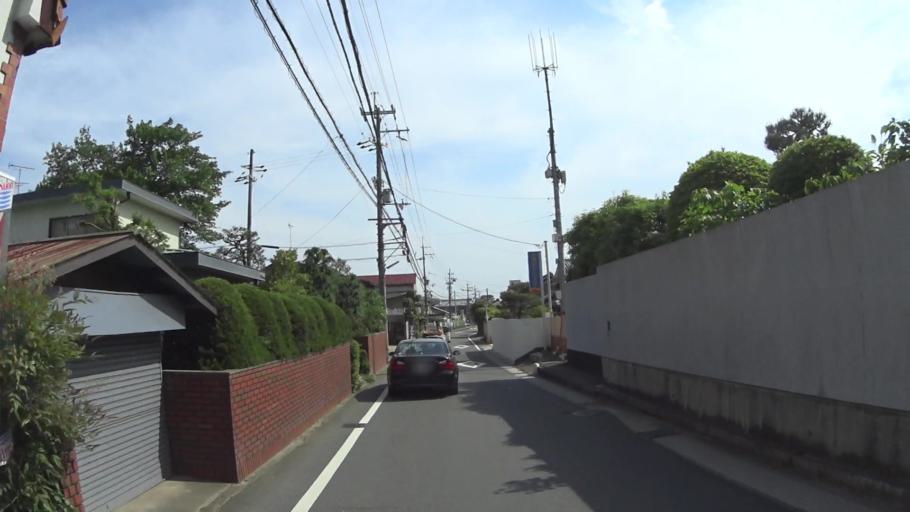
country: JP
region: Shiga Prefecture
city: Otsu-shi
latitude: 34.9722
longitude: 135.8216
